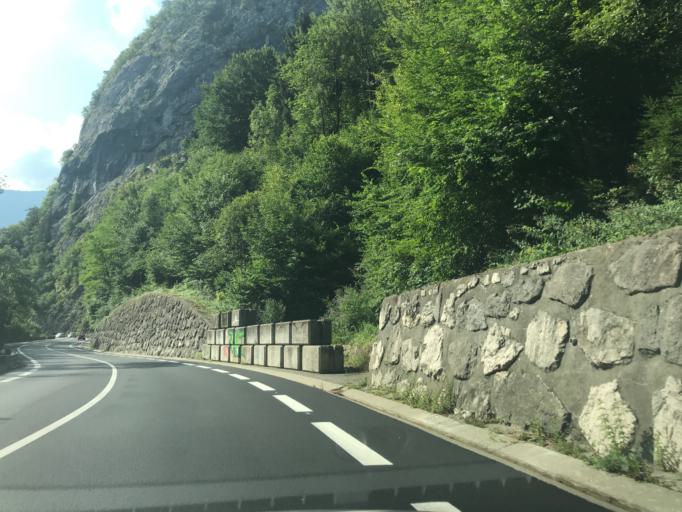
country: FR
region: Rhone-Alpes
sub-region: Departement de la Haute-Savoie
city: Dingy-Saint-Clair
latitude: 45.9071
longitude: 6.2035
